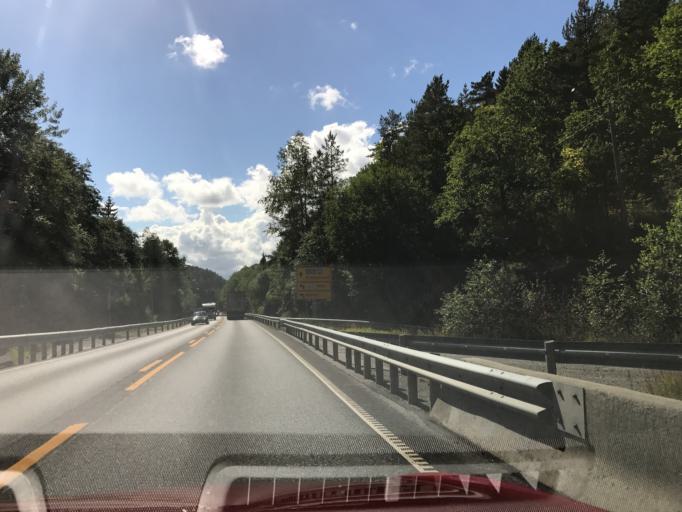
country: NO
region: Telemark
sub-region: Kragero
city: Kragero
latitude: 58.9655
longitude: 9.4845
